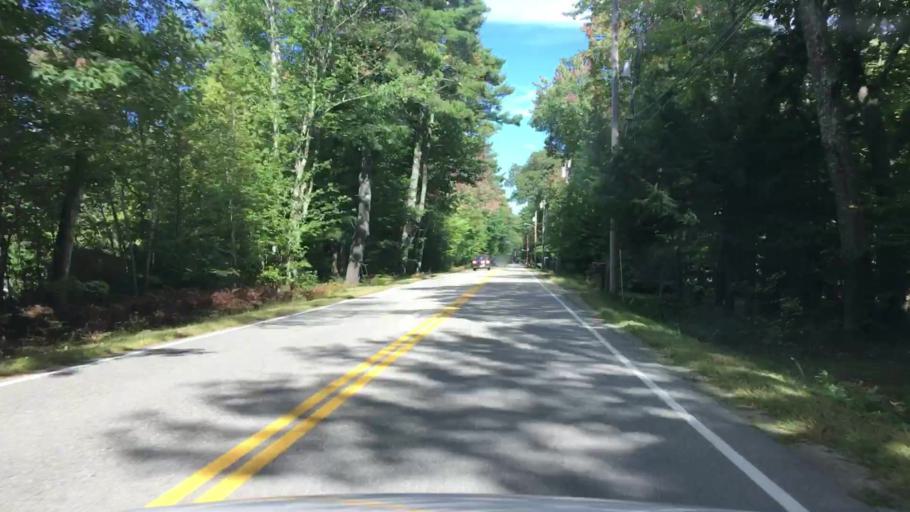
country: US
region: Maine
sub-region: Cumberland County
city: Westbrook
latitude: 43.6344
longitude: -70.4048
